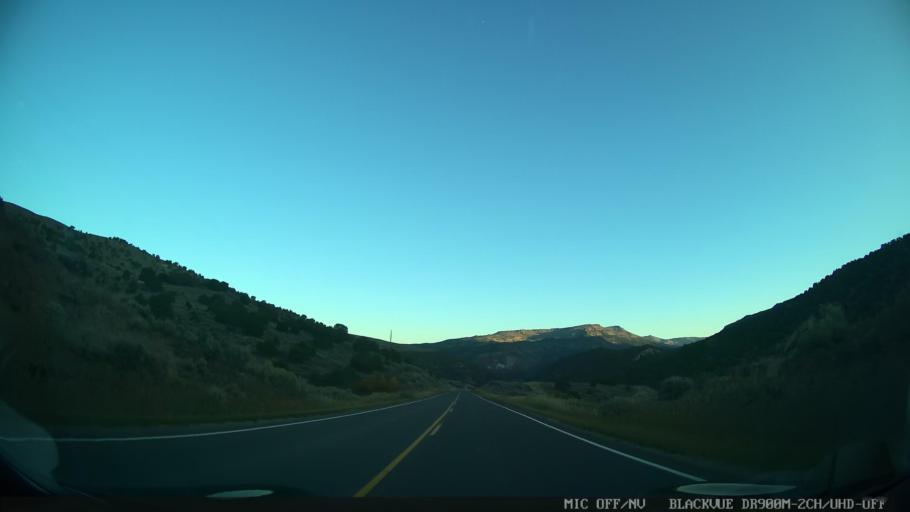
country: US
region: Colorado
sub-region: Eagle County
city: Edwards
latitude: 39.8366
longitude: -106.6393
